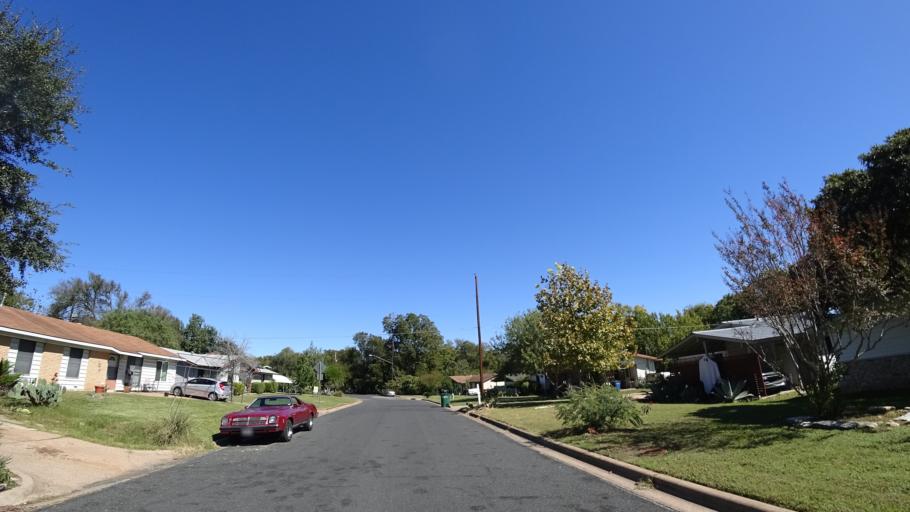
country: US
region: Texas
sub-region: Travis County
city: Rollingwood
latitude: 30.2187
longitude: -97.7814
